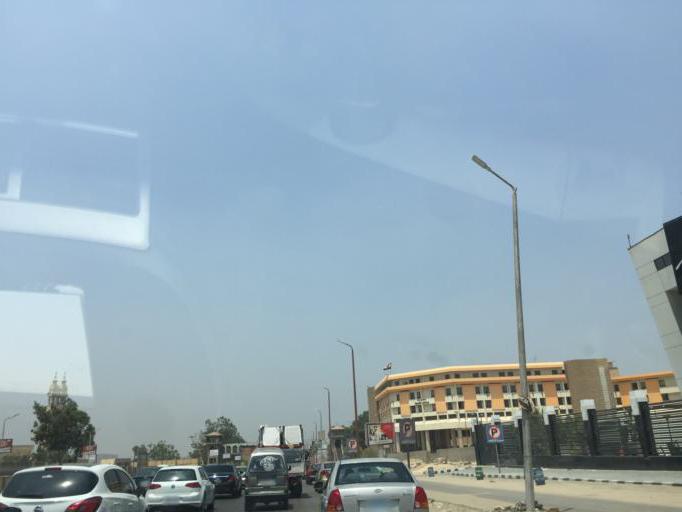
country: EG
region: Muhafazat al Qahirah
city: Cairo
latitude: 30.0789
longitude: 31.3753
